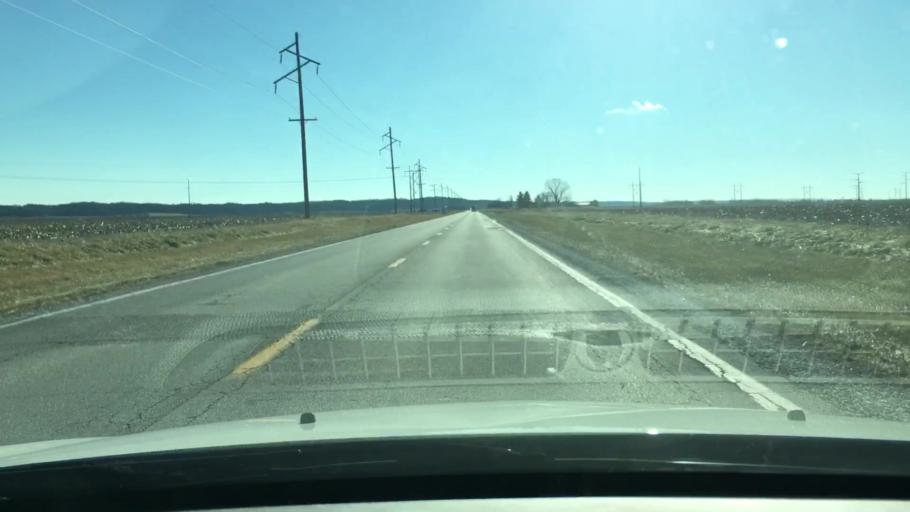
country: US
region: Illinois
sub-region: Morgan County
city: Meredosia
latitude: 39.8706
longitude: -90.5053
